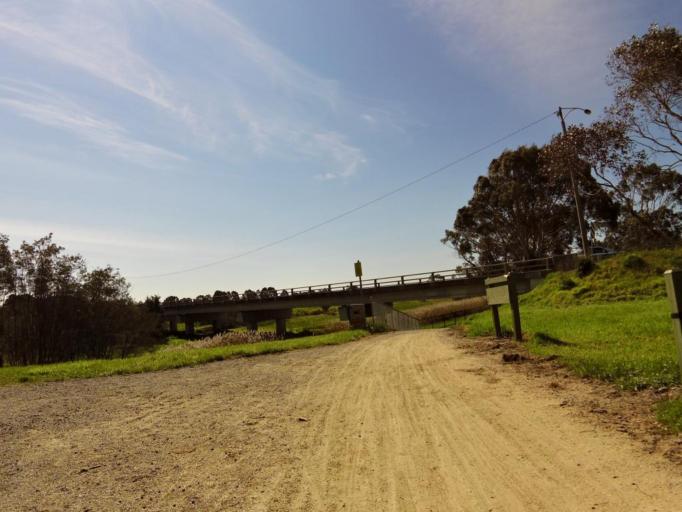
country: AU
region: Victoria
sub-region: Greater Dandenong
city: Keysborough
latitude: -38.0331
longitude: 145.1841
